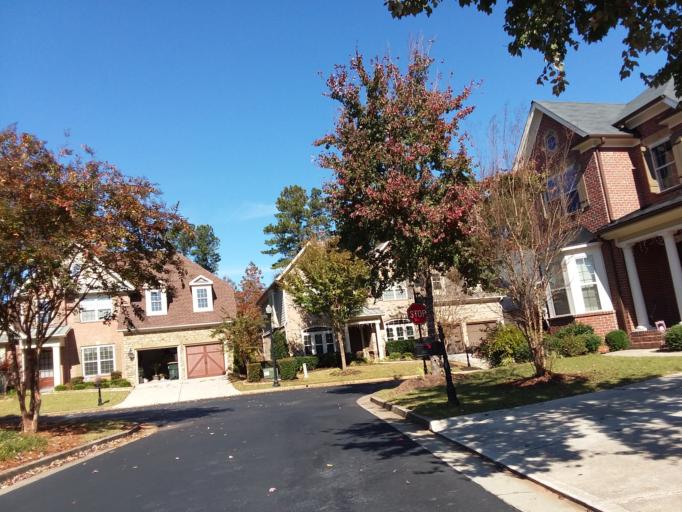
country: US
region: Georgia
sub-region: Fulton County
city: Johns Creek
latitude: 34.0256
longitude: -84.2538
